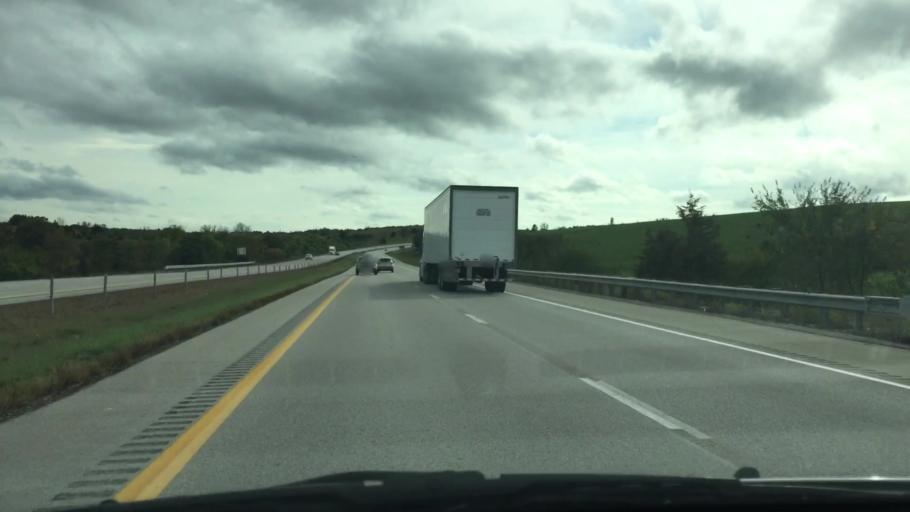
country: US
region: Iowa
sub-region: Clarke County
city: Osceola
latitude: 41.0598
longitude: -93.7818
